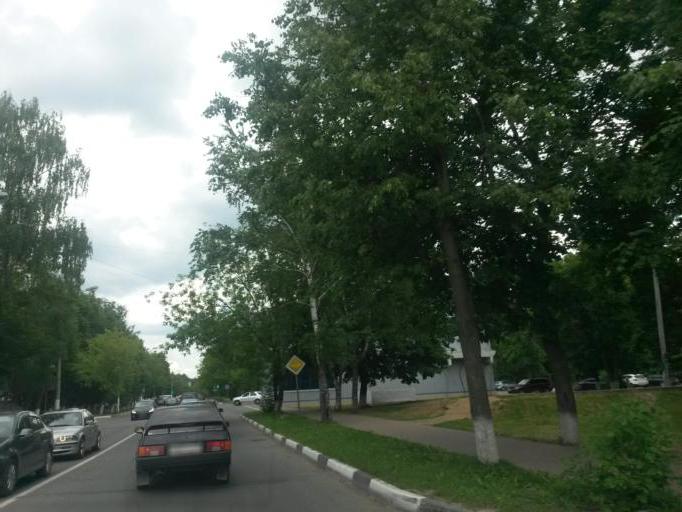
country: RU
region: Moskovskaya
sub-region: Chekhovskiy Rayon
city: Chekhov
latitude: 55.1566
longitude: 37.4638
